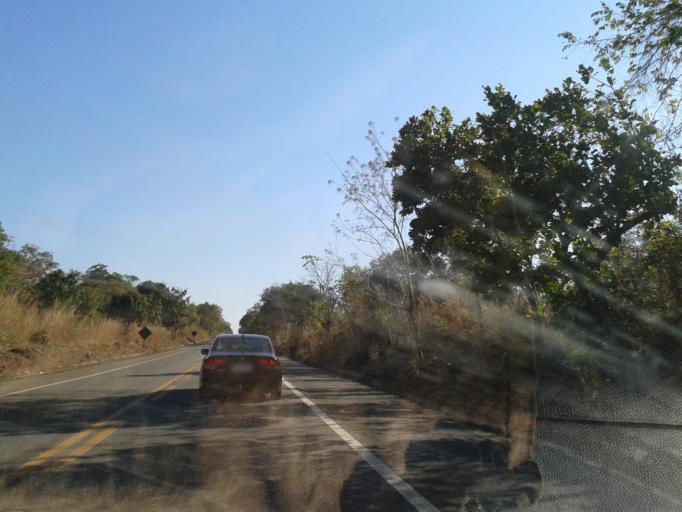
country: BR
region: Goias
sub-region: Mozarlandia
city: Mozarlandia
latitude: -14.8200
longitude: -50.5309
